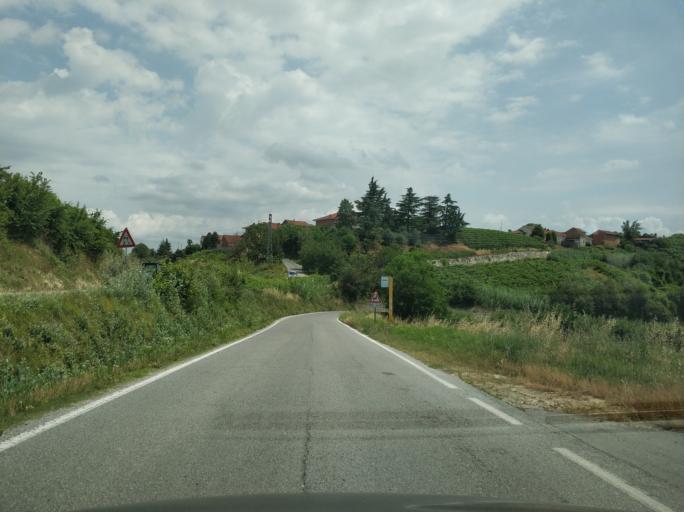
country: IT
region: Piedmont
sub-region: Provincia di Cuneo
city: Santo Stefano Roero
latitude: 44.7869
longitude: 7.9539
